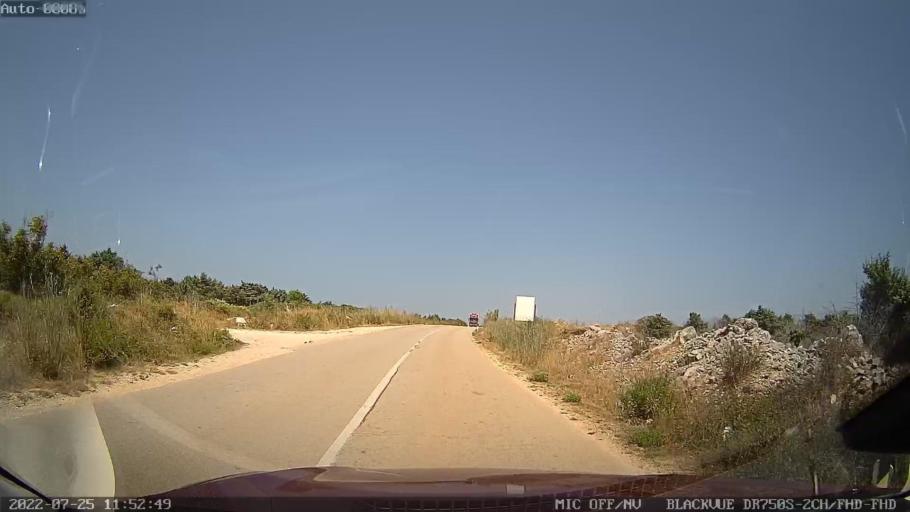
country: HR
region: Zadarska
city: Vrsi
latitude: 44.2508
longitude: 15.2396
